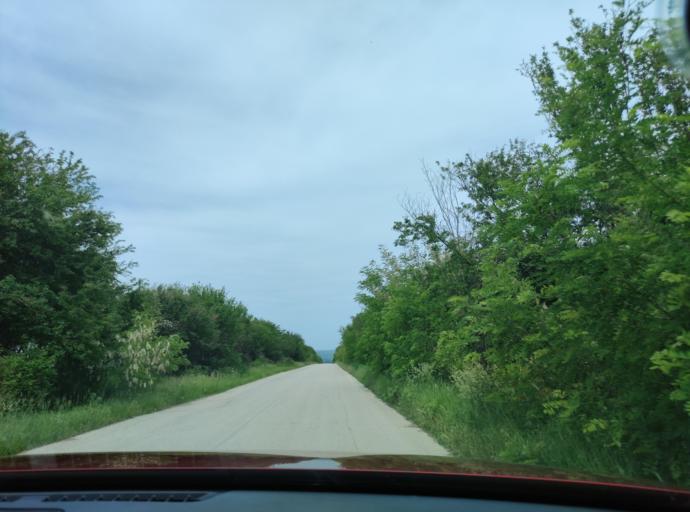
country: BG
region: Pleven
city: Iskur
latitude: 43.5266
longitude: 24.3146
